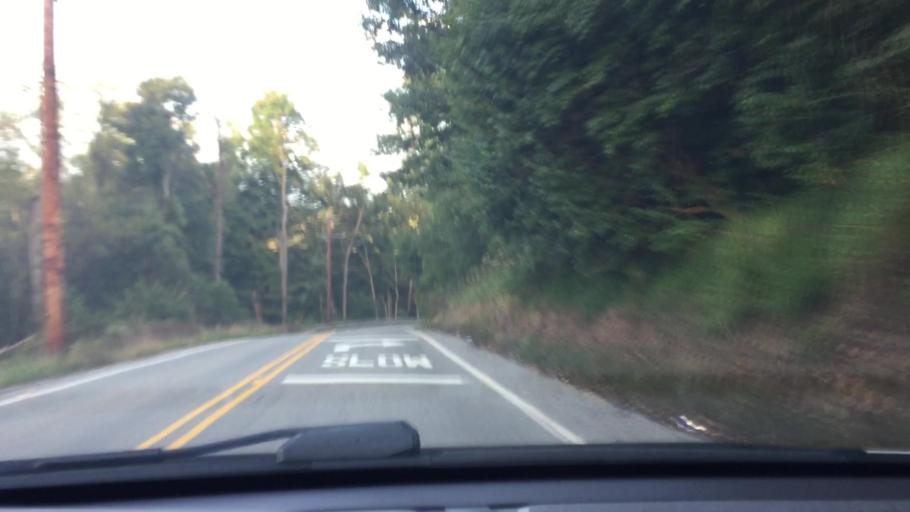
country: US
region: Pennsylvania
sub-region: Allegheny County
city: Plum
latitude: 40.4577
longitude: -79.7403
